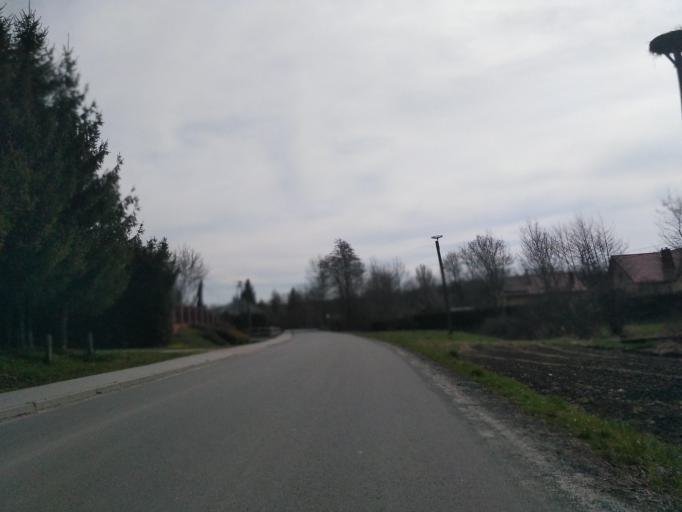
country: PL
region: Subcarpathian Voivodeship
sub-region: Powiat ropczycko-sedziszowski
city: Iwierzyce
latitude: 50.0202
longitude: 21.7891
